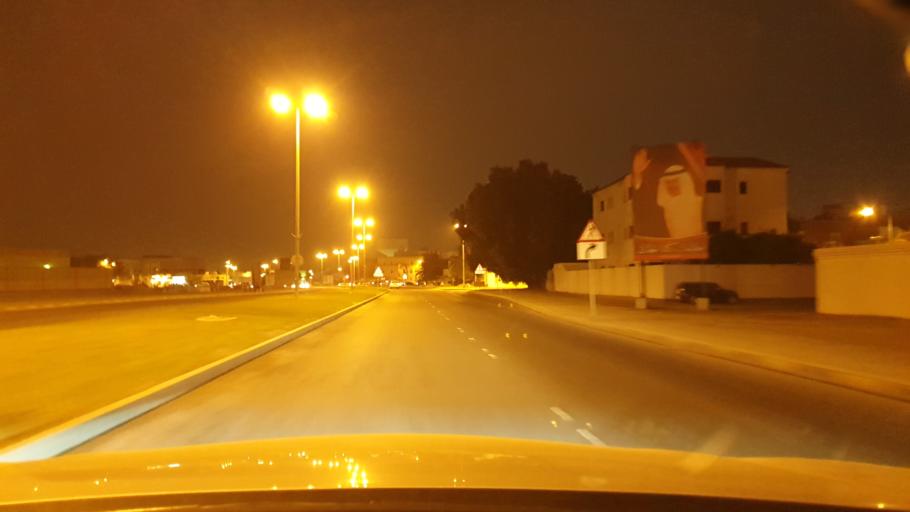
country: BH
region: Muharraq
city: Al Hadd
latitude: 26.2602
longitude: 50.6397
